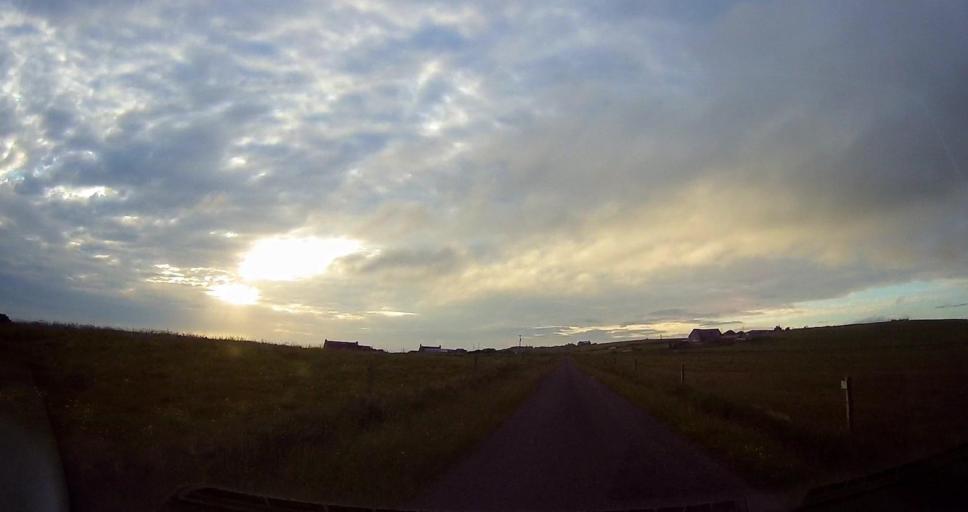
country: GB
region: Scotland
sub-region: Orkney Islands
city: Stromness
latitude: 59.1224
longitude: -3.2775
